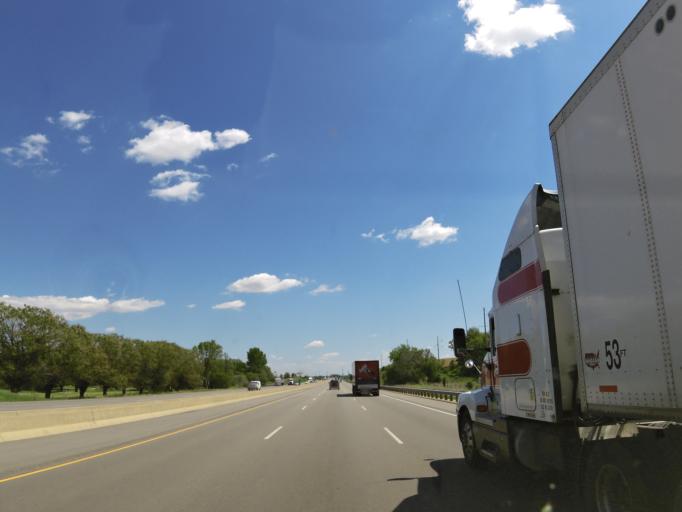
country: US
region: Wisconsin
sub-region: Dane County
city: Windsor
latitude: 43.2040
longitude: -89.3539
